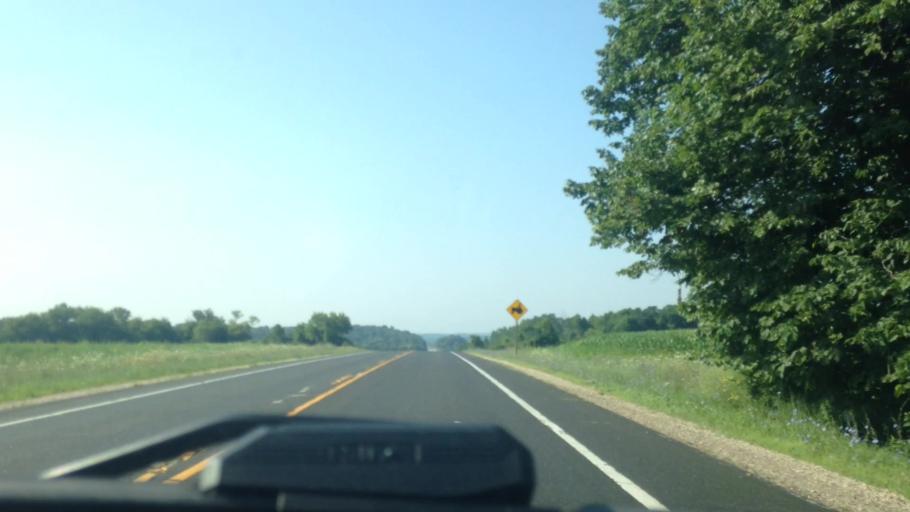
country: US
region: Wisconsin
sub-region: Washington County
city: Richfield
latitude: 43.2153
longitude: -88.2617
